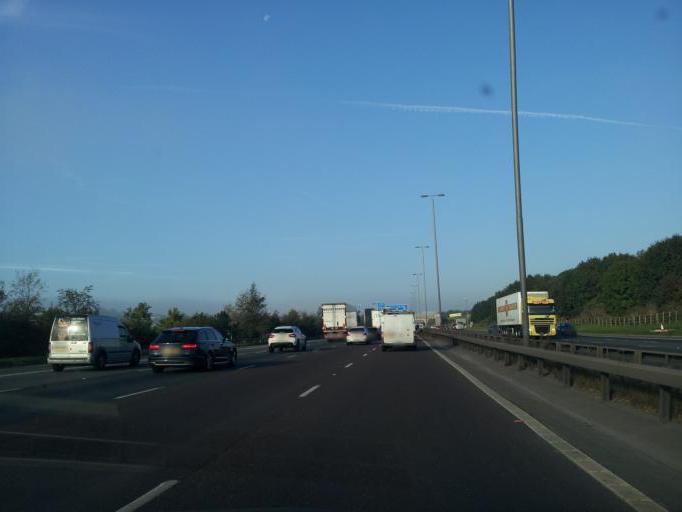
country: GB
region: England
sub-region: City and Borough of Leeds
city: Morley
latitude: 53.7332
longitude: -1.5483
